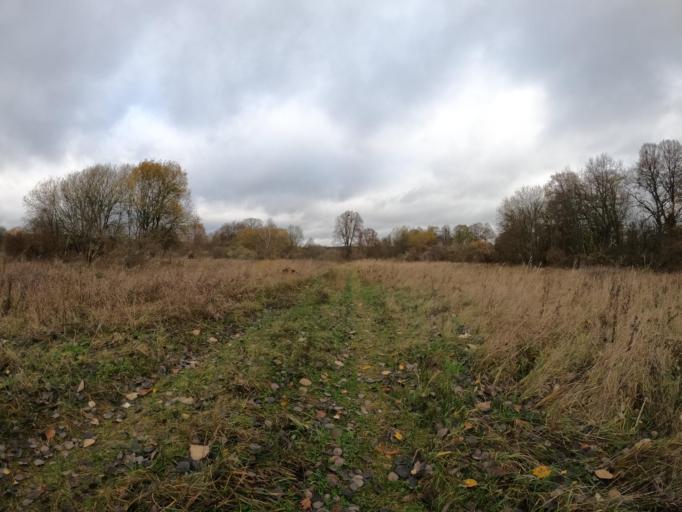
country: PL
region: West Pomeranian Voivodeship
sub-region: Powiat walecki
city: Miroslawiec
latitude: 53.3145
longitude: 16.1109
